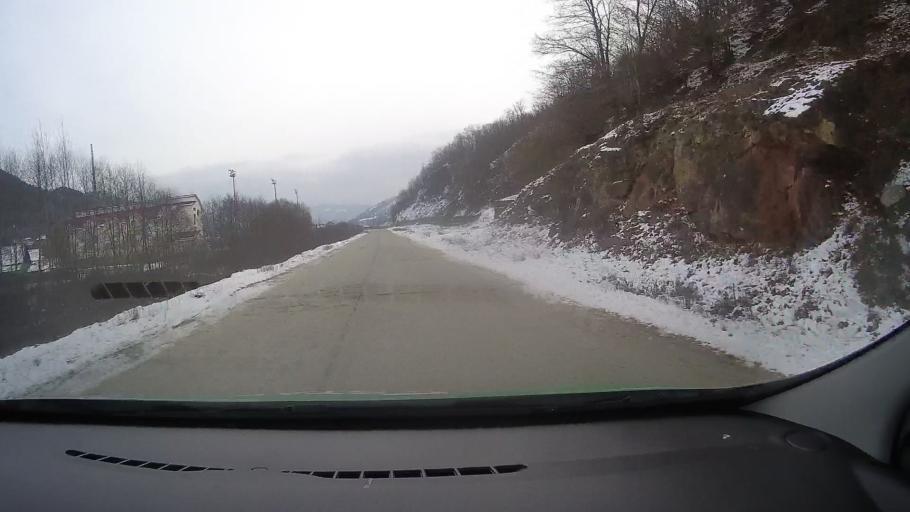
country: RO
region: Alba
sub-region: Oras Zlatna
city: Zlatna
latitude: 46.1158
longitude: 23.2087
